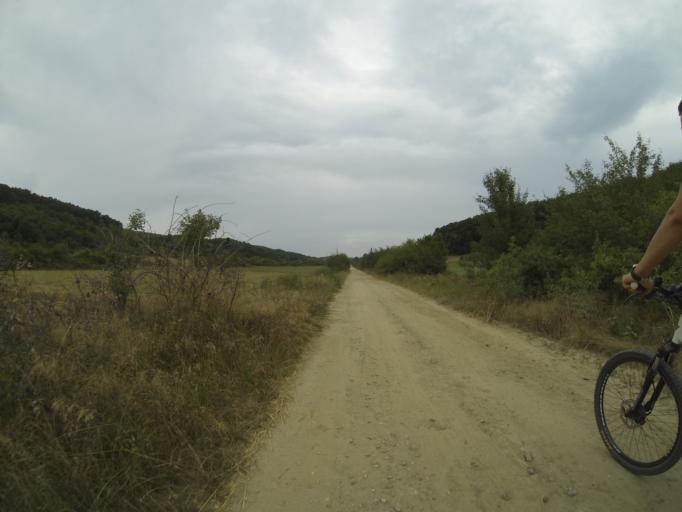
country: RO
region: Dolj
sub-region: Comuna Bradesti
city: Bradesti
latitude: 44.5123
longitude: 23.6400
